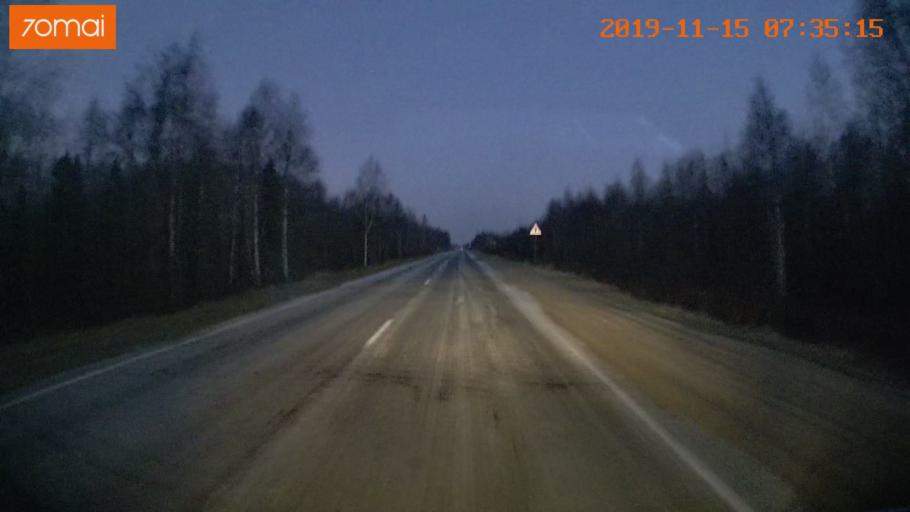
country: RU
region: Vologda
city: Sheksna
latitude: 58.7284
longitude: 38.4547
